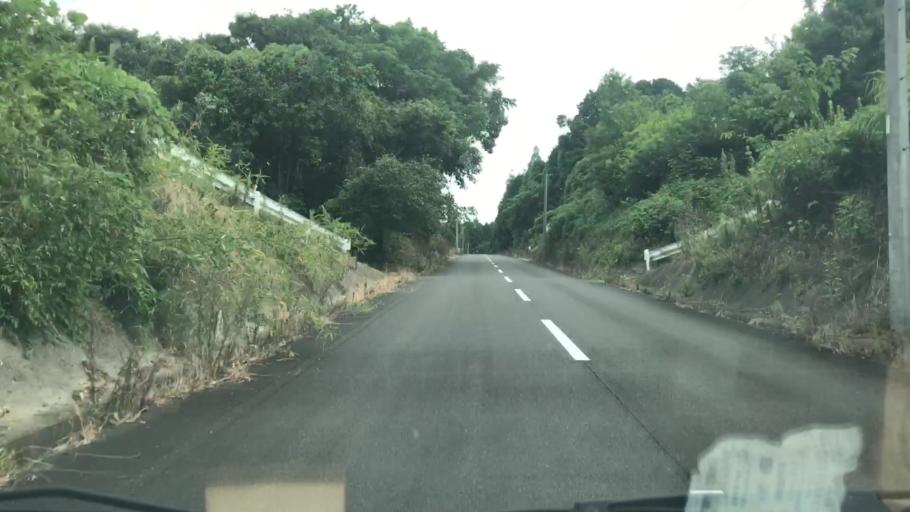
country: JP
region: Saga Prefecture
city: Takeocho-takeo
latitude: 33.2247
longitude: 129.9779
